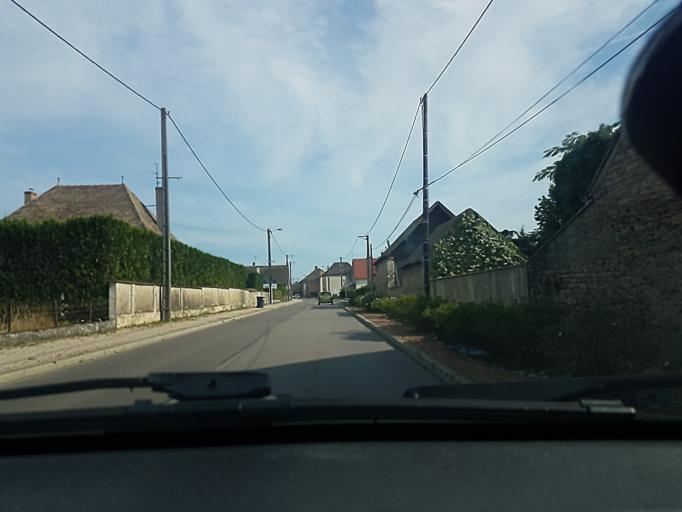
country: FR
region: Bourgogne
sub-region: Departement de Saone-et-Loire
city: Epervans
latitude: 46.7560
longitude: 4.8962
